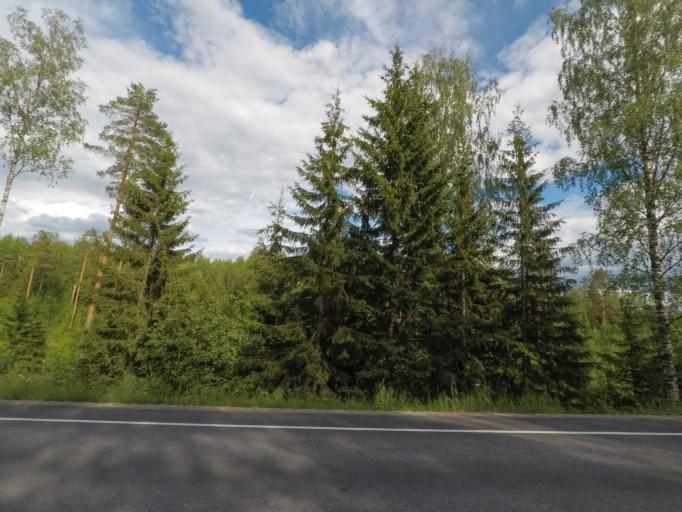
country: FI
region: Uusimaa
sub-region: Porvoo
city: Pukkila
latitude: 60.7832
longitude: 25.4592
